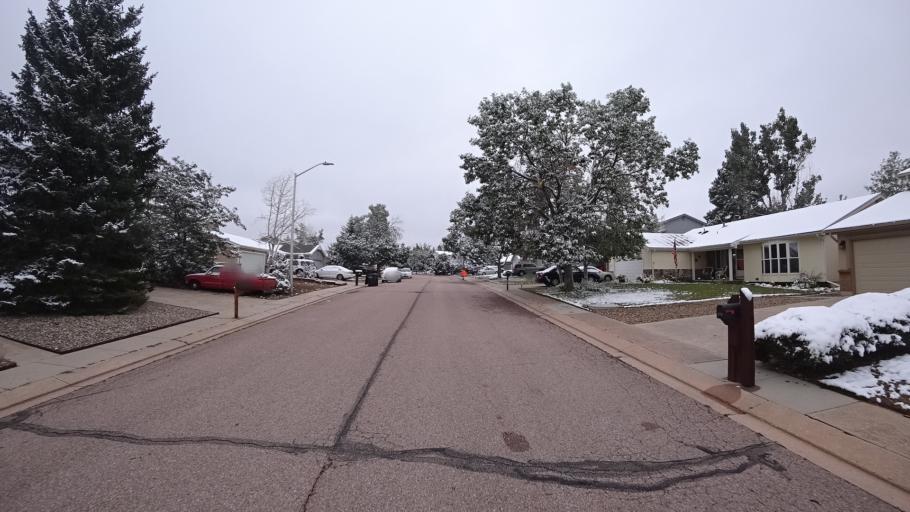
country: US
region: Colorado
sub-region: El Paso County
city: Colorado Springs
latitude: 38.9237
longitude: -104.7770
